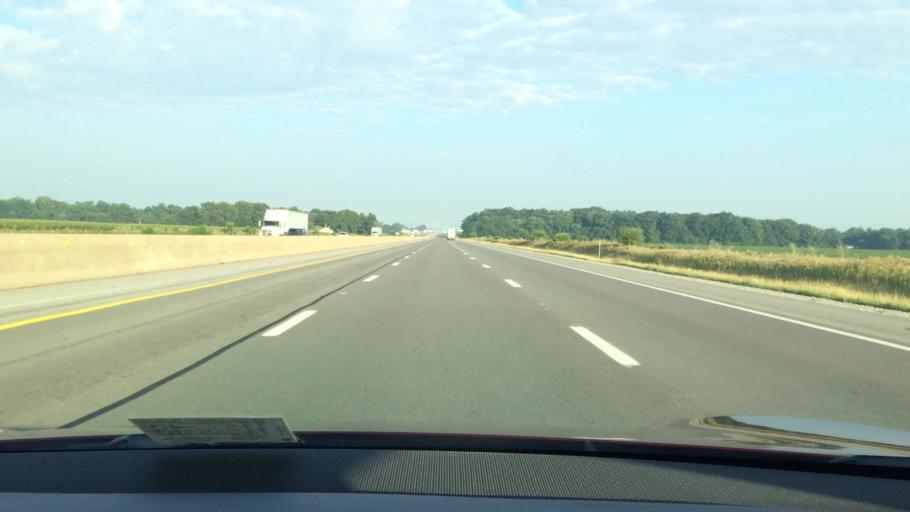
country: US
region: Ohio
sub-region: Huron County
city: Monroeville
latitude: 41.3370
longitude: -82.7328
